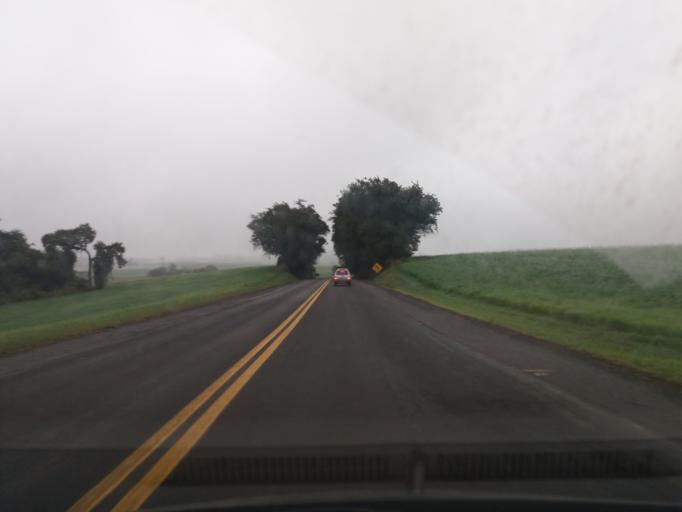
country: BR
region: Parana
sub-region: Realeza
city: Realeza
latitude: -25.8065
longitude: -53.5218
